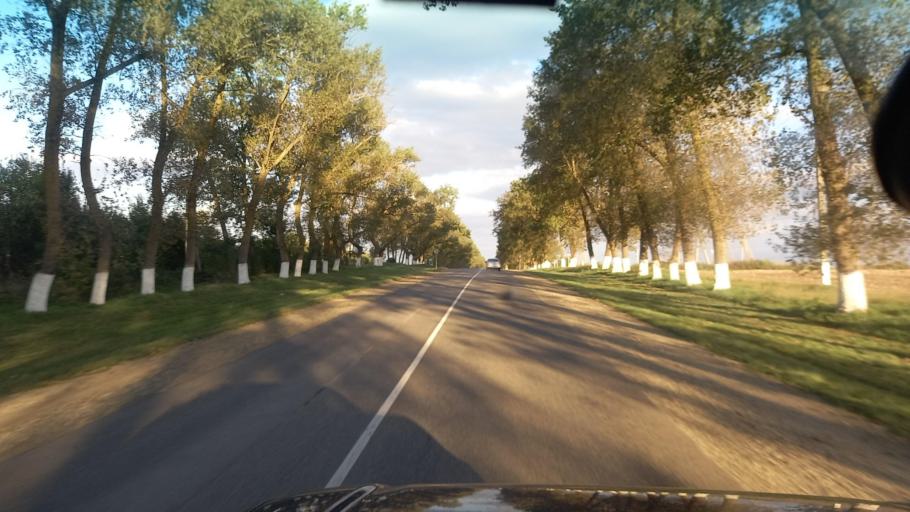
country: RU
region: Krasnodarskiy
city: Krymsk
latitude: 44.9399
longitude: 37.9312
